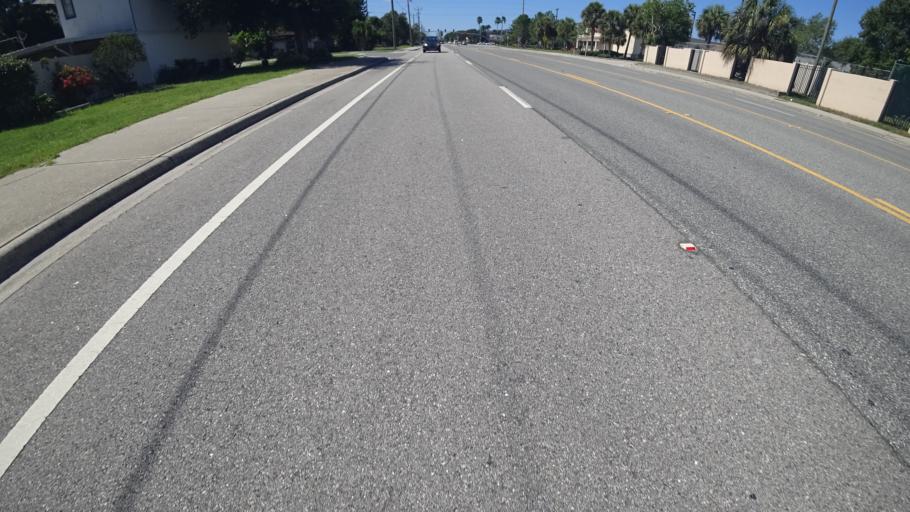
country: US
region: Florida
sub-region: Manatee County
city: South Bradenton
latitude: 27.4495
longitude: -82.5958
